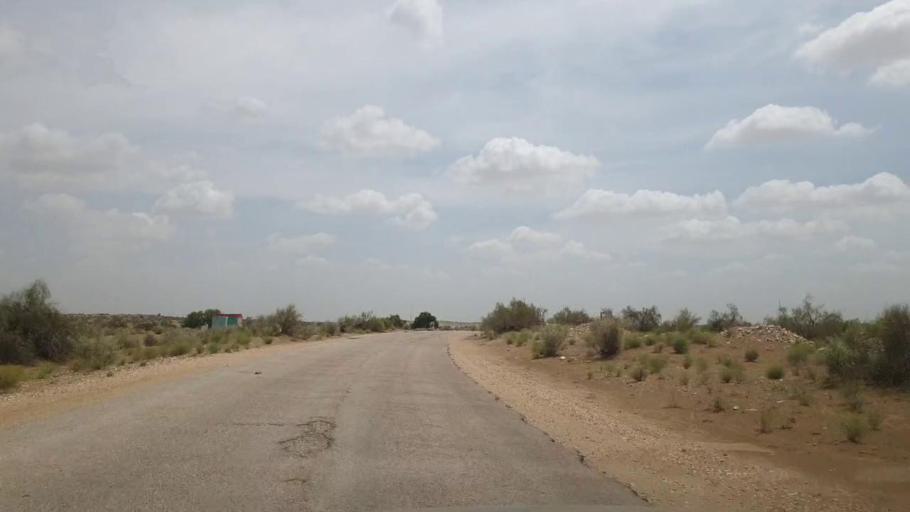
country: PK
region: Sindh
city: Kot Diji
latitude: 27.1525
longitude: 69.2265
